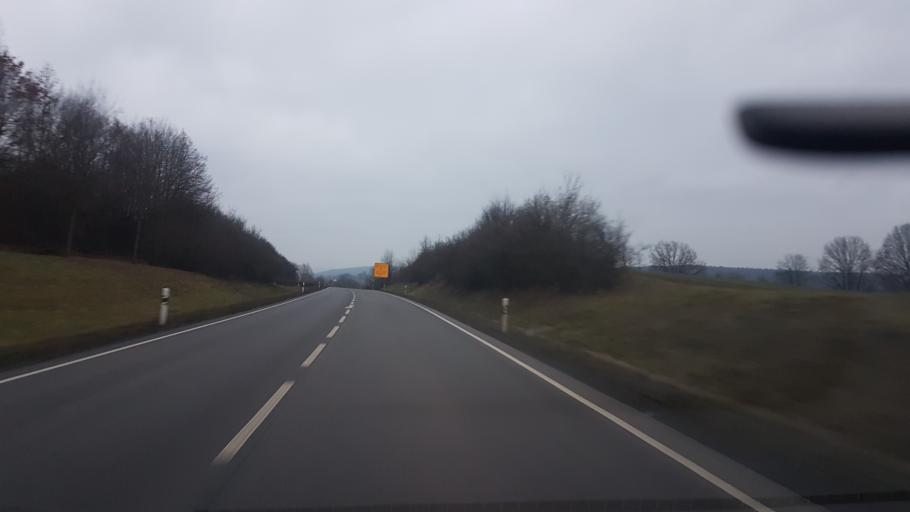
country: DE
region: Bavaria
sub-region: Upper Franconia
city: Reckendorf
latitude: 50.0294
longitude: 10.8266
